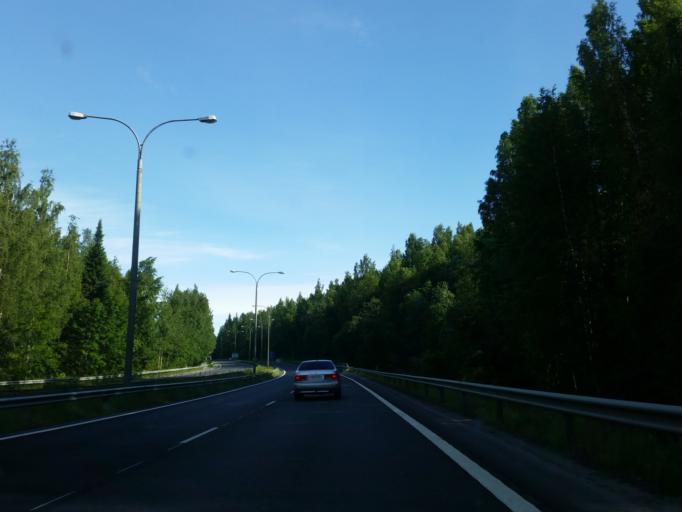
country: FI
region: Northern Savo
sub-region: Kuopio
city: Kuopio
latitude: 62.9172
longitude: 27.6787
